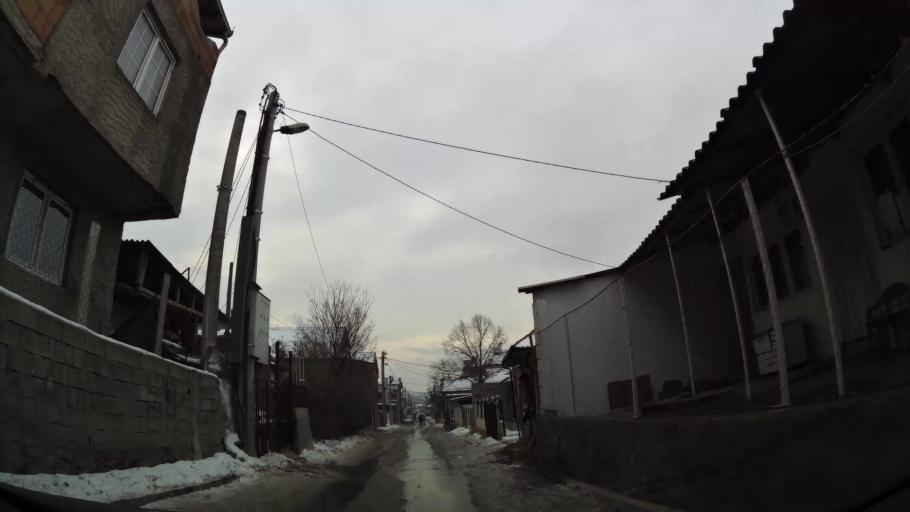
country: MK
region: Suto Orizari
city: Suto Orizare
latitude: 42.0471
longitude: 21.4212
